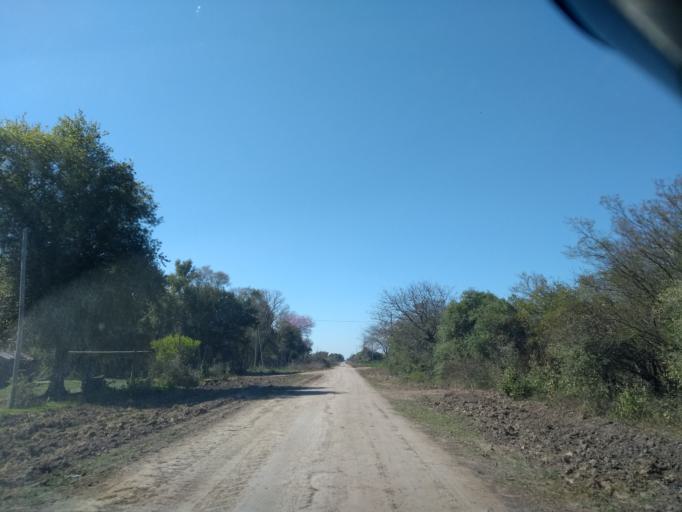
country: AR
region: Chaco
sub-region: Departamento de Quitilipi
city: Quitilipi
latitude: -26.7453
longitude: -60.2765
